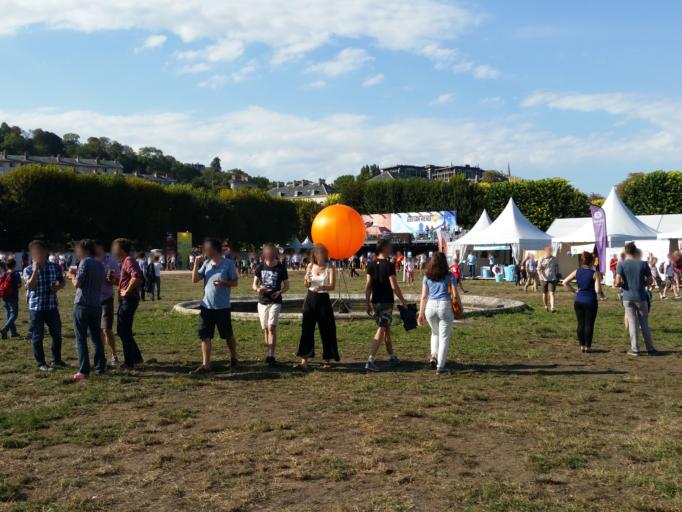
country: FR
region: Ile-de-France
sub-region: Departement des Hauts-de-Seine
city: Sevres
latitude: 48.8366
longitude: 2.2212
